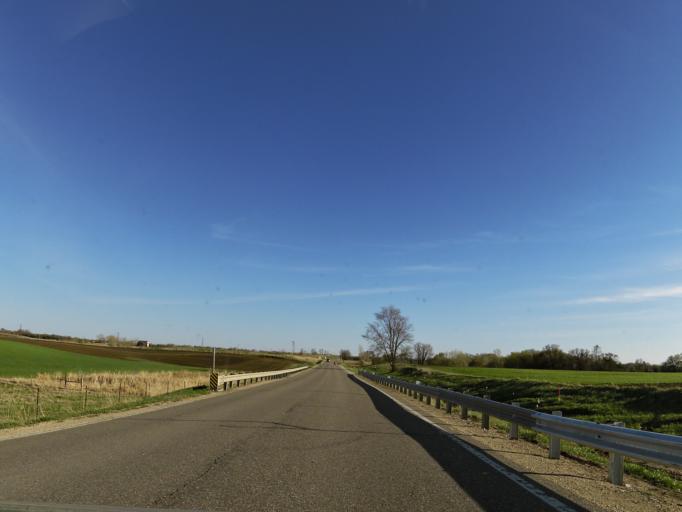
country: US
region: Minnesota
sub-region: Dakota County
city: Lakeville
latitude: 44.6155
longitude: -93.2633
